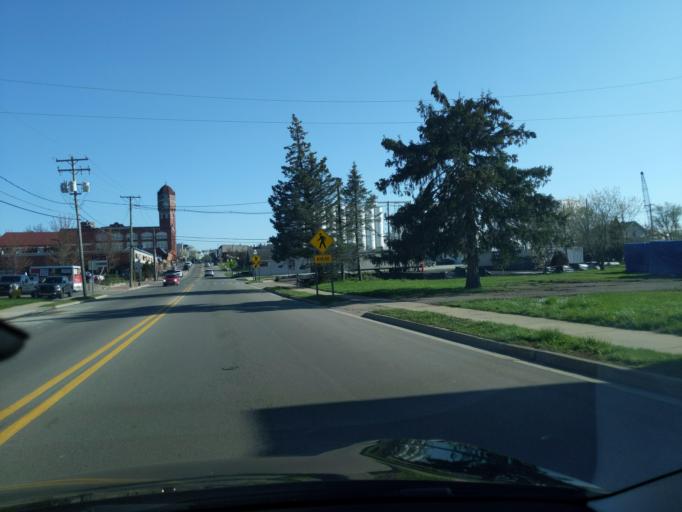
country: US
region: Michigan
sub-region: Washtenaw County
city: Chelsea
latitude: 42.3217
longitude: -84.0206
